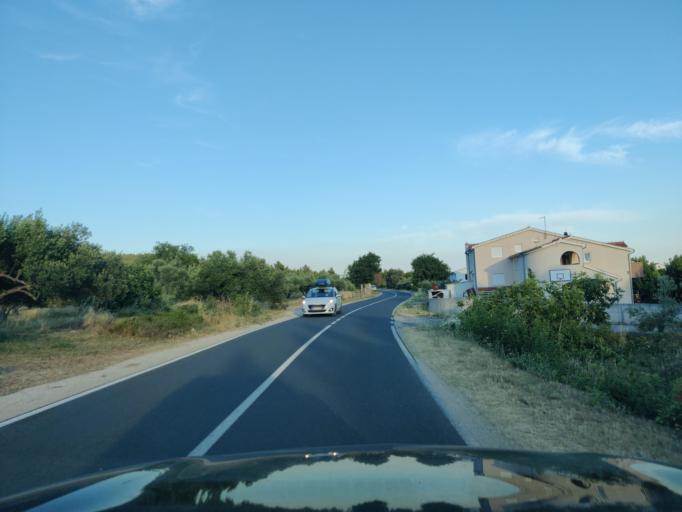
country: HR
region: Sibensko-Kniniska
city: Tribunj
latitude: 43.7671
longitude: 15.7327
